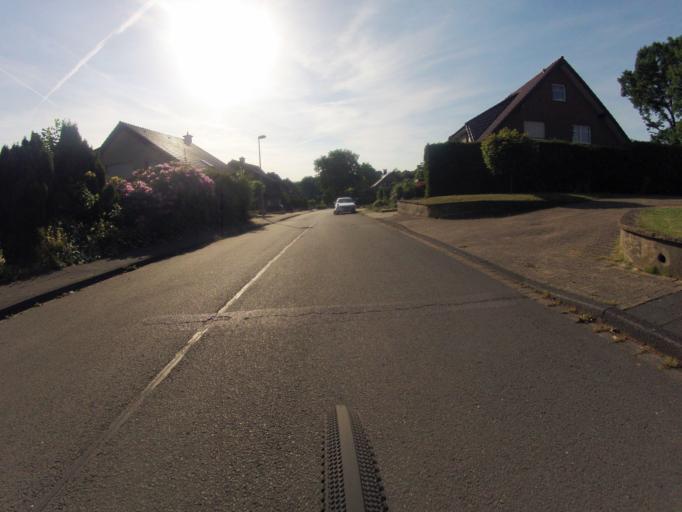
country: DE
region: North Rhine-Westphalia
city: Ibbenburen
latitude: 52.2918
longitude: 7.7054
